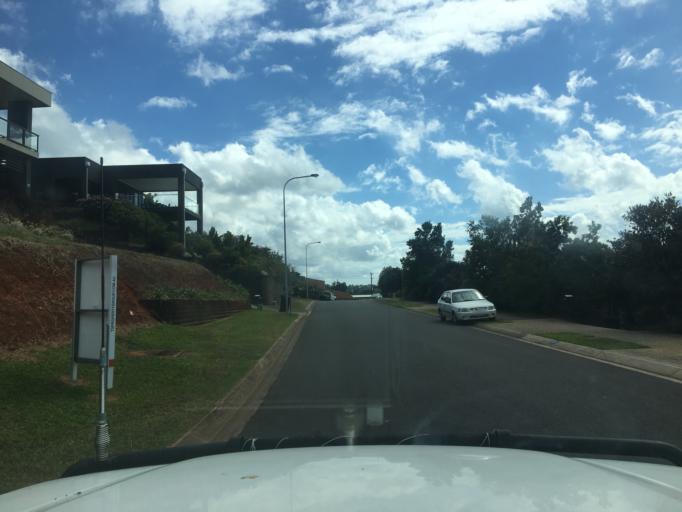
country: AU
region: Queensland
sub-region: Cairns
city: Woree
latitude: -16.9687
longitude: 145.7397
